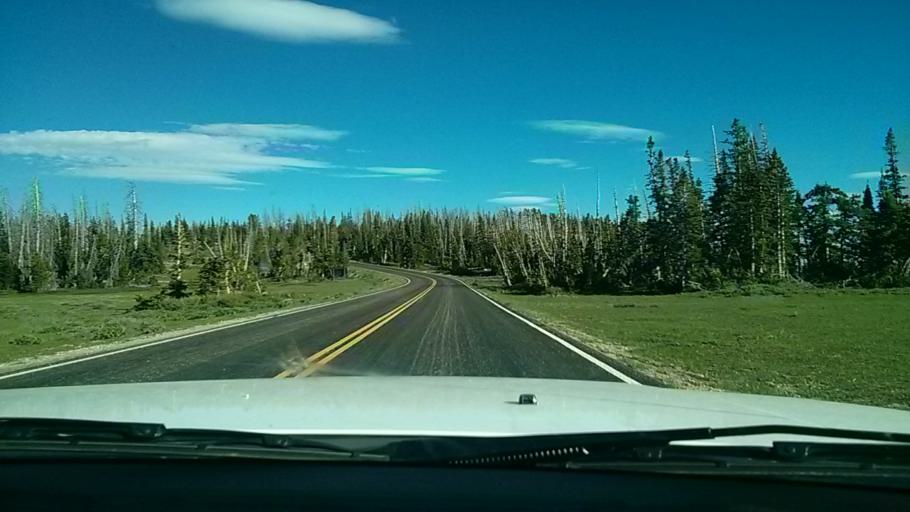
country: US
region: Utah
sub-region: Iron County
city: Parowan
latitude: 37.6290
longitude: -112.8293
